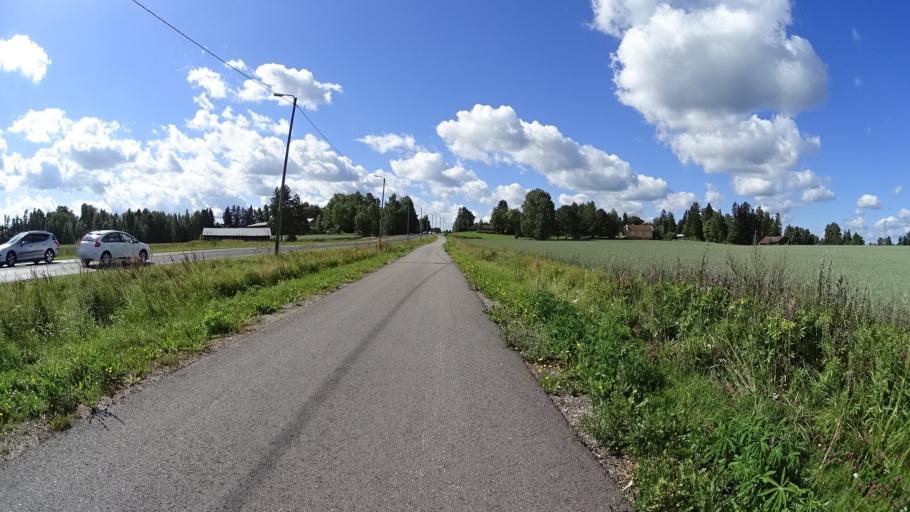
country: FI
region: Uusimaa
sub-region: Helsinki
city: Jaervenpaeae
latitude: 60.4413
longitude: 25.0730
